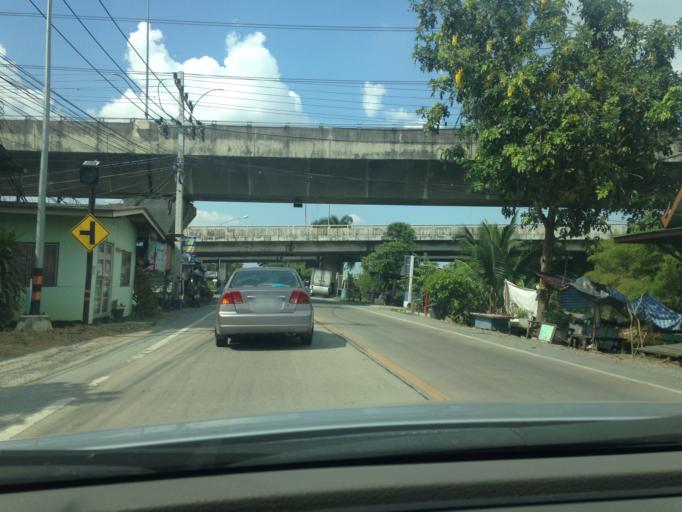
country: TH
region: Pathum Thani
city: Khlong Luang
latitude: 14.0650
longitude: 100.5887
